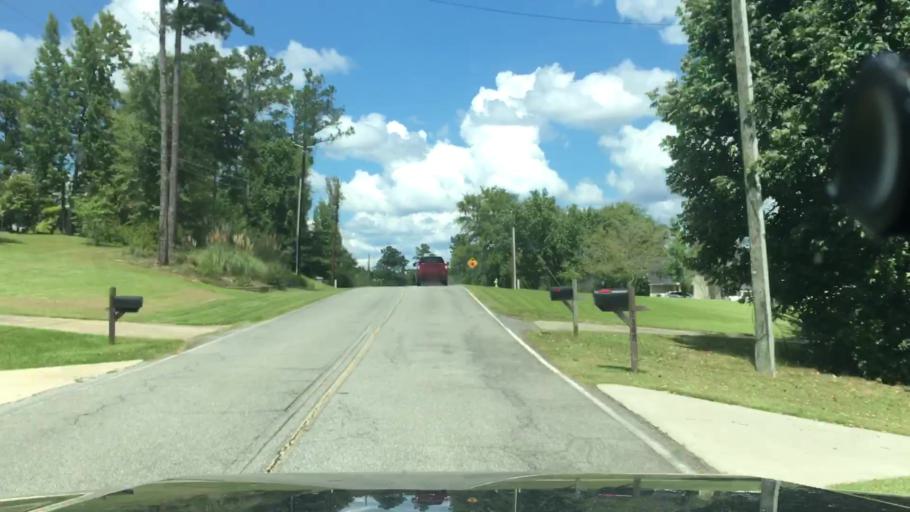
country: US
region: Georgia
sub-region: Bibb County
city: West Point
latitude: 32.8129
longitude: -83.7917
